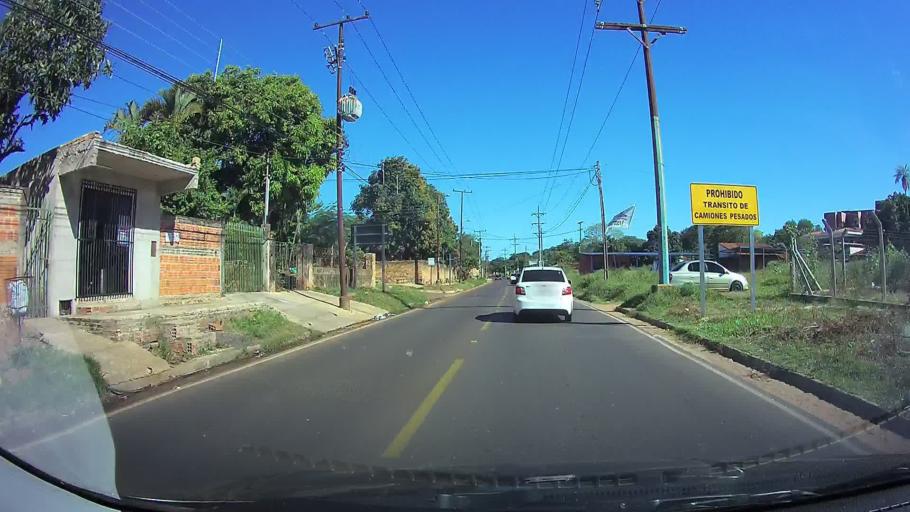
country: PY
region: Central
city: Fernando de la Mora
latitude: -25.3139
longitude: -57.5234
